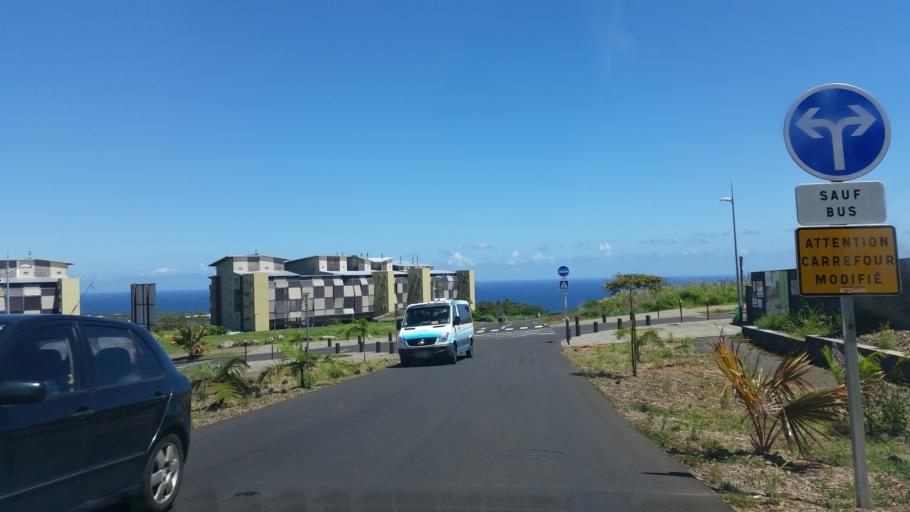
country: RE
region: Reunion
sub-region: Reunion
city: Sainte-Marie
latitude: -20.9179
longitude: 55.5280
